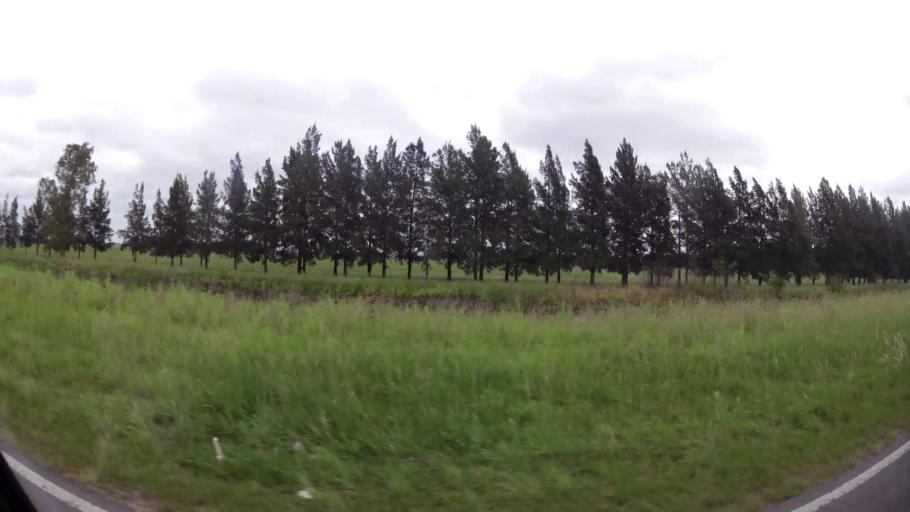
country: AR
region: Buenos Aires
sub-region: Partido de San Vicente
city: San Vicente
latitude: -35.0377
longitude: -58.4556
